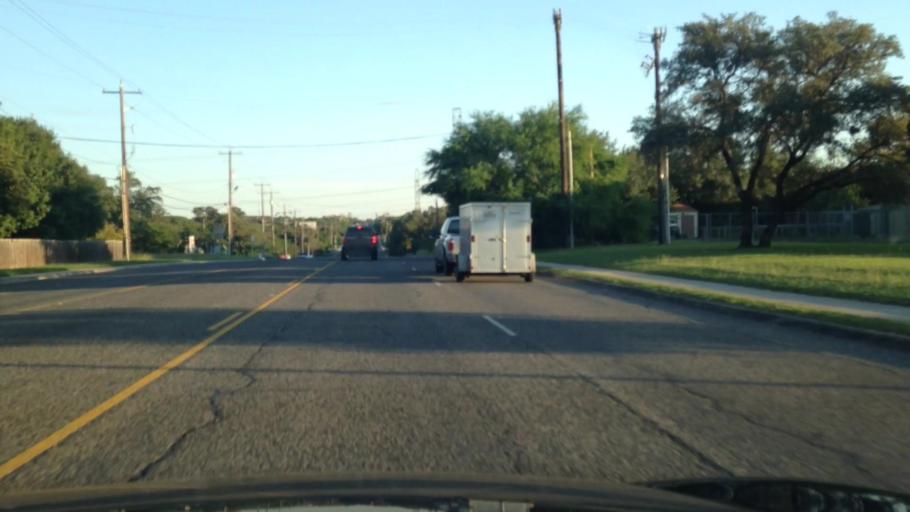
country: US
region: Texas
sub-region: Bexar County
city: Live Oak
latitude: 29.5963
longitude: -98.3836
